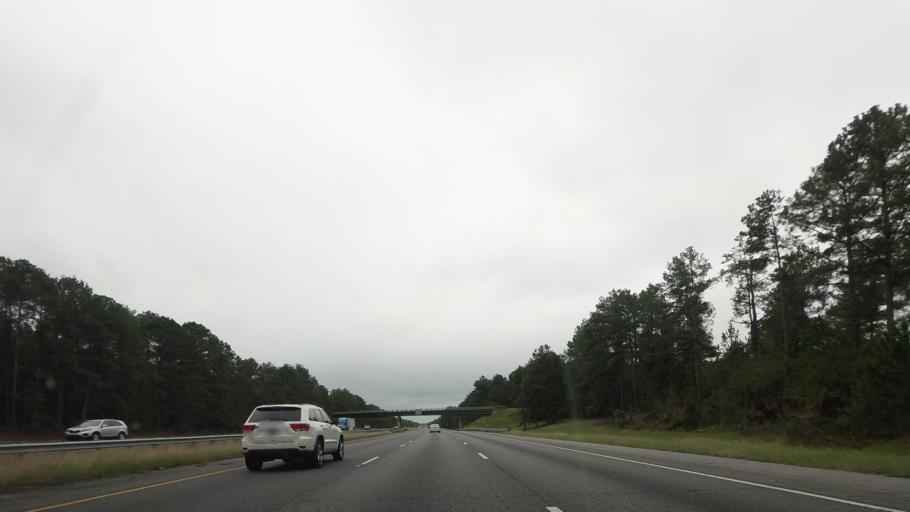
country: US
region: Georgia
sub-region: Houston County
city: Perry
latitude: 32.3838
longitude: -83.7682
